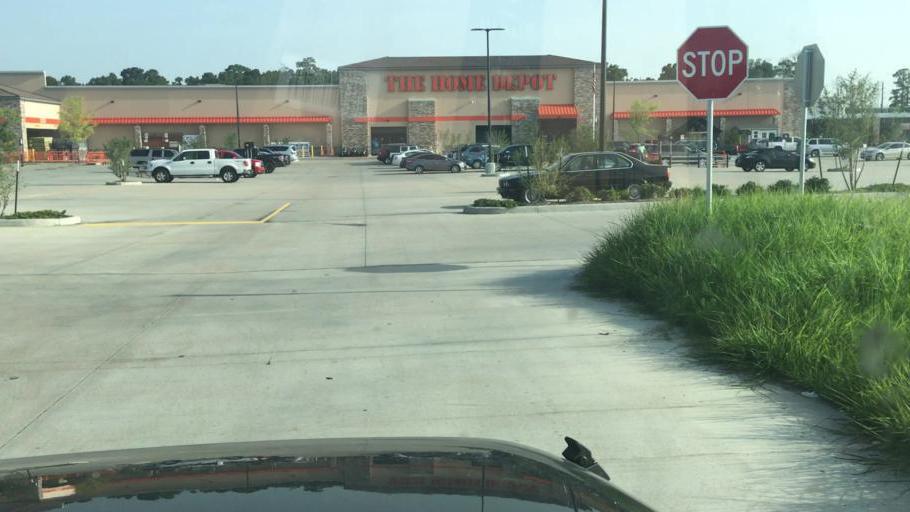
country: US
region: Texas
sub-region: Harris County
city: Atascocita
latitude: 29.9231
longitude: -95.1949
